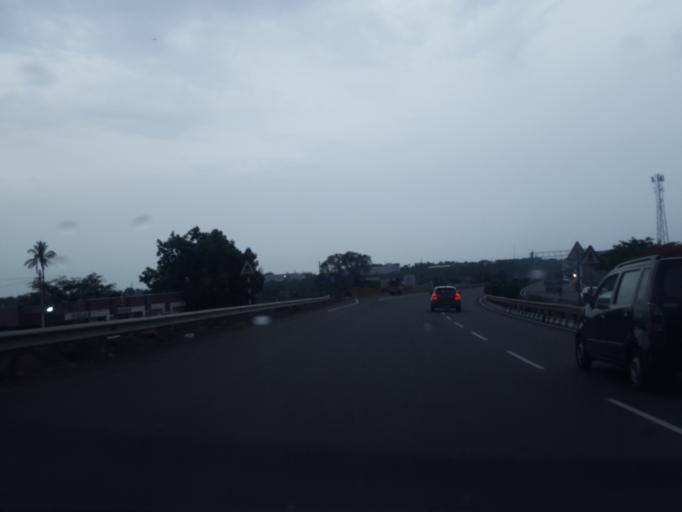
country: IN
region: Telangana
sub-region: Mahbubnagar
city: Farrukhnagar
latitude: 17.1436
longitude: 78.2918
